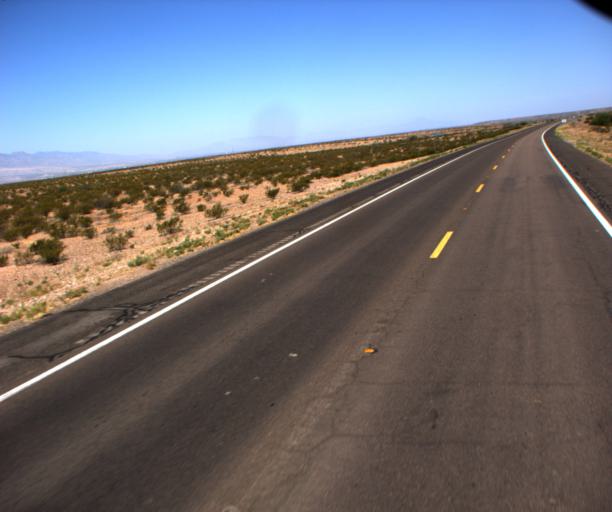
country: US
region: Arizona
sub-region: Graham County
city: Safford
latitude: 32.8050
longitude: -109.5799
